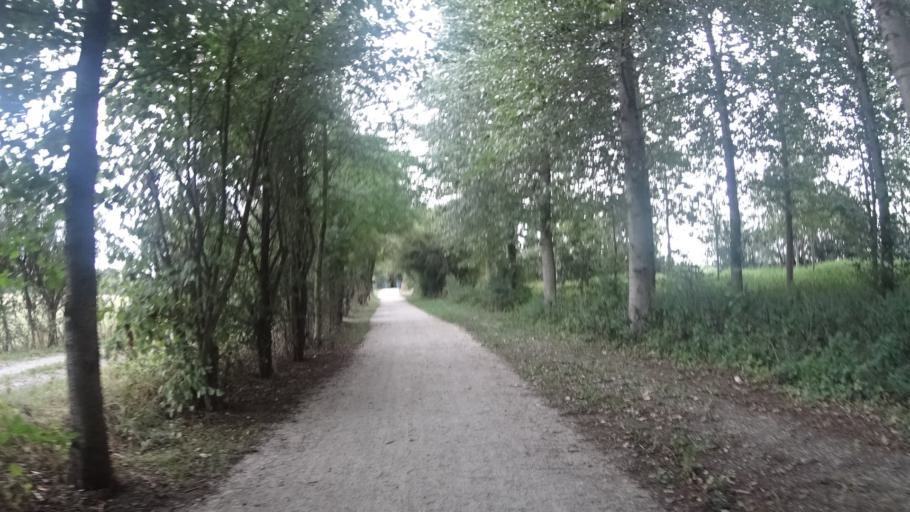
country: FR
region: Picardie
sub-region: Departement de l'Aisne
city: Origny-Sainte-Benoite
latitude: 49.8489
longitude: 3.4973
